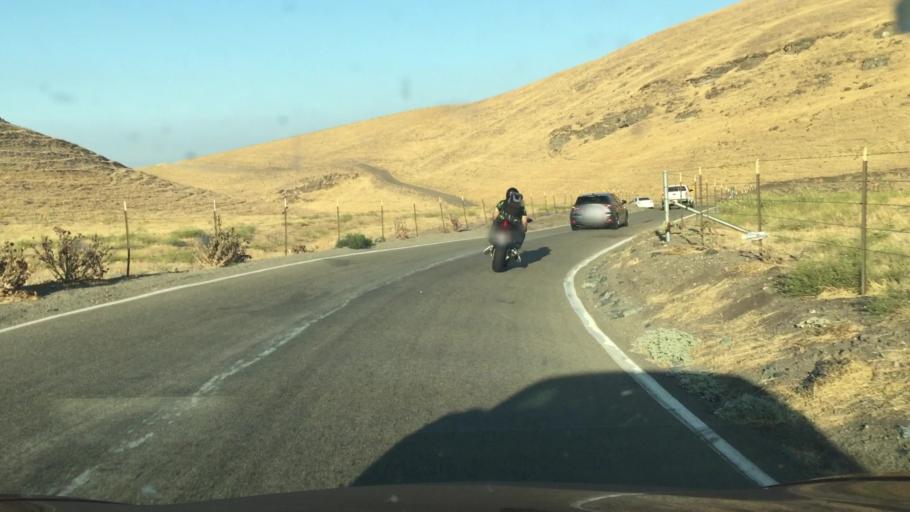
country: US
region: California
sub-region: San Joaquin County
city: Mountain House
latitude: 37.6975
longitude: -121.5887
